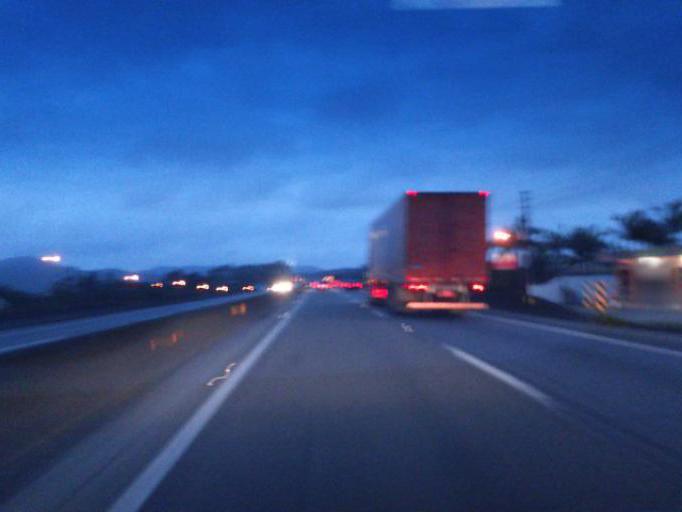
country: BR
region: Santa Catarina
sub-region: Penha
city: Penha
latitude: -26.7633
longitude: -48.6866
